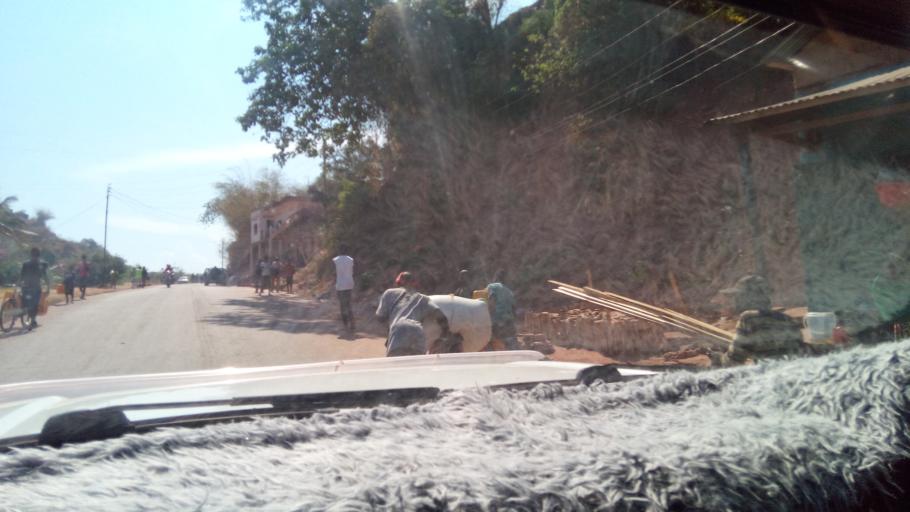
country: CD
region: Katanga
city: Kalemie
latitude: -5.9381
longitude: 29.1928
